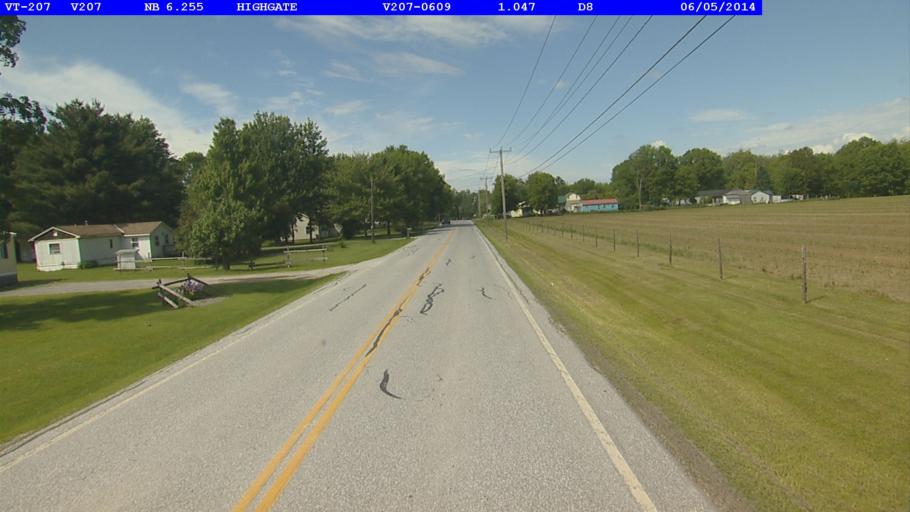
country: US
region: Vermont
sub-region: Franklin County
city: Swanton
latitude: 44.9258
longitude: -73.0511
